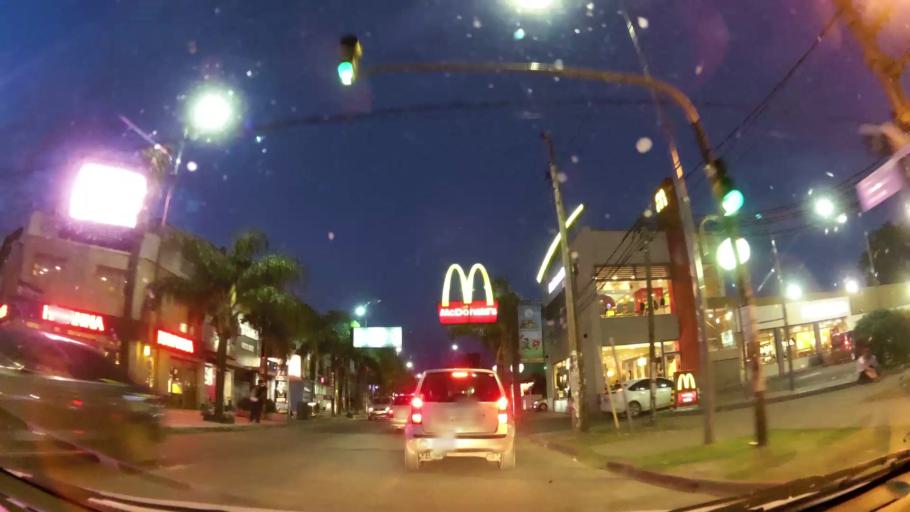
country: AR
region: Buenos Aires
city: Ituzaingo
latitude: -34.6428
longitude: -58.6566
